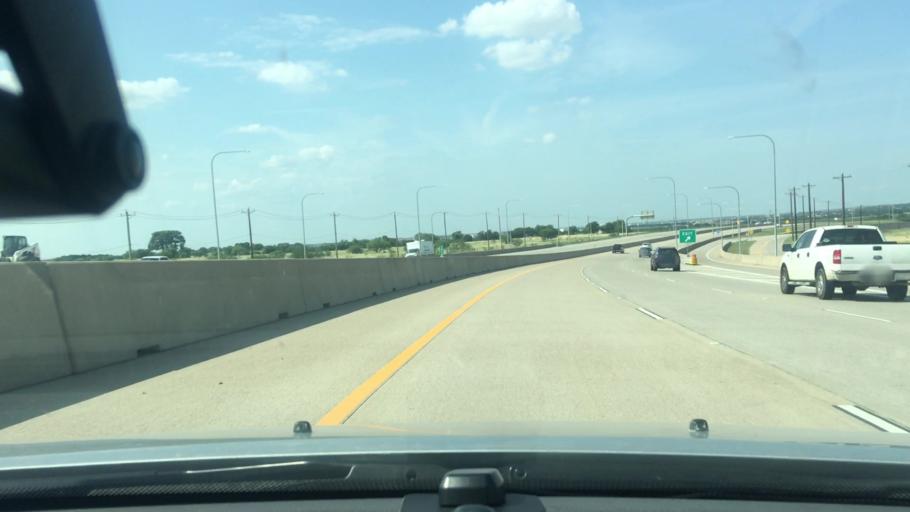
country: US
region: Texas
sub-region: Collin County
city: Frisco
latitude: 33.1916
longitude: -96.8387
